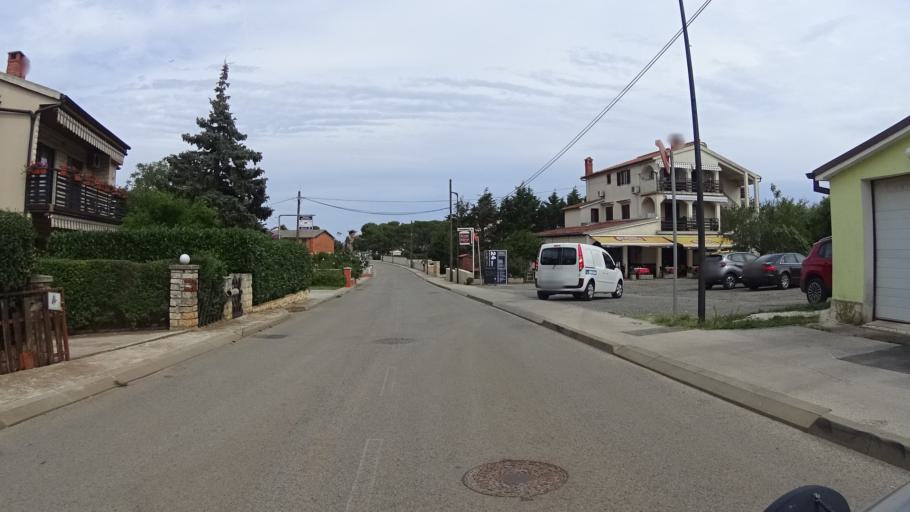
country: HR
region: Istarska
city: Medulin
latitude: 44.8250
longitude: 13.8932
